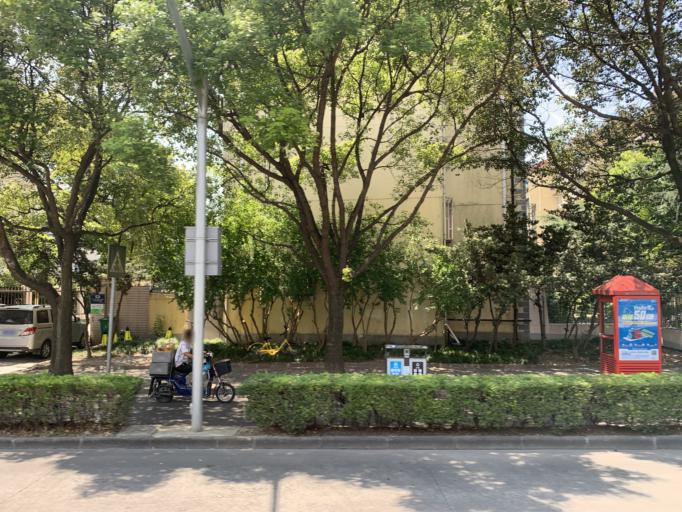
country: CN
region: Shanghai Shi
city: Huamu
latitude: 31.2511
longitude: 121.5784
